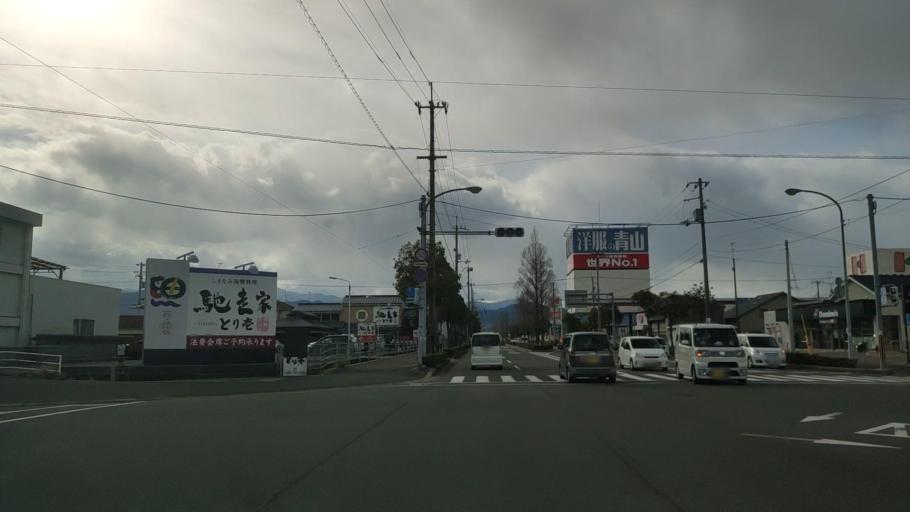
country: JP
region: Ehime
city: Saijo
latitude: 34.0485
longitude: 133.0094
